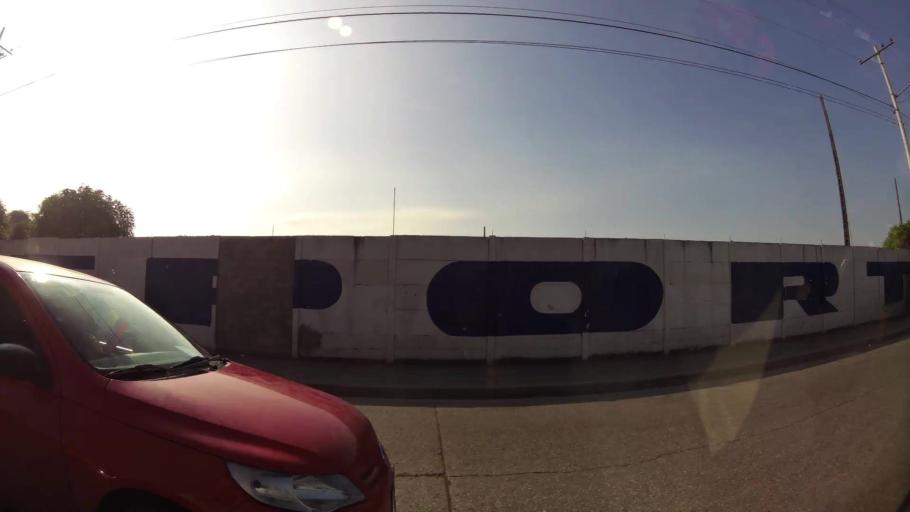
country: EC
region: Guayas
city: Eloy Alfaro
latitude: -2.1757
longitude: -79.8434
